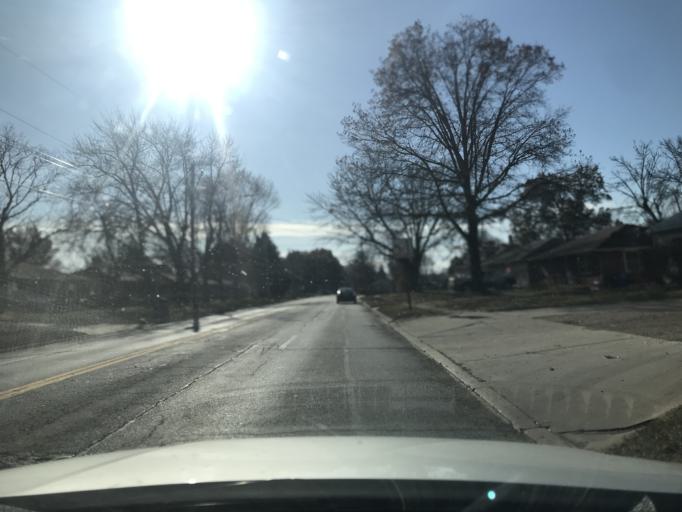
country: US
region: Iowa
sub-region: Scott County
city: Davenport
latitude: 41.5324
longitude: -90.6133
